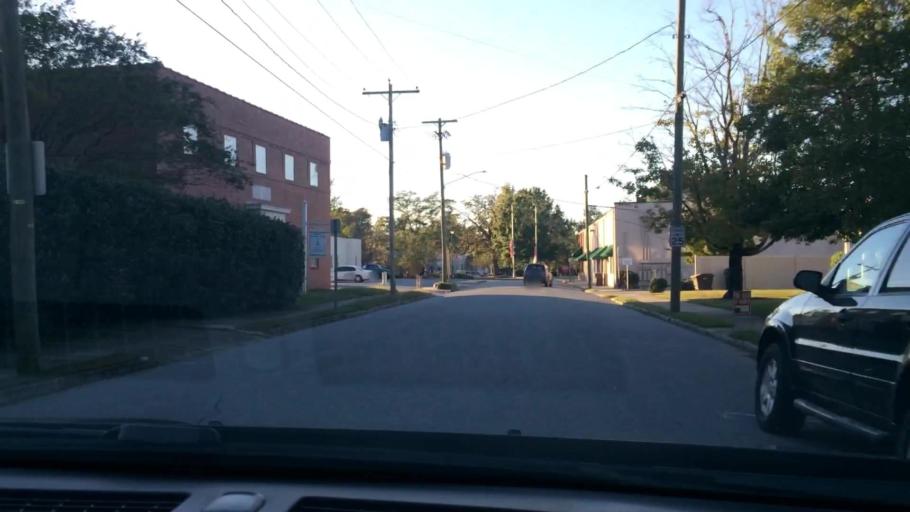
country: US
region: North Carolina
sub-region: Pitt County
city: Farmville
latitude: 35.5977
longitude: -77.5831
